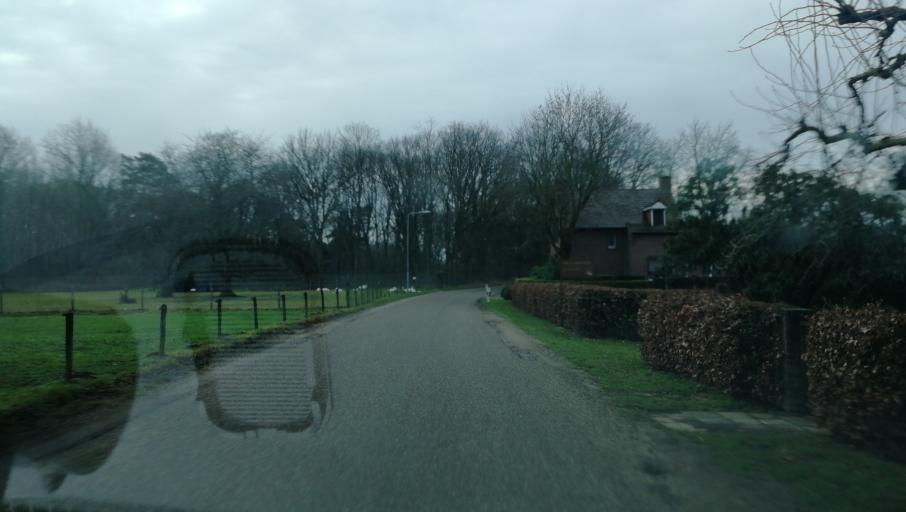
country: NL
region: Limburg
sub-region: Gemeente Venlo
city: Venlo
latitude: 51.4116
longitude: 6.1924
